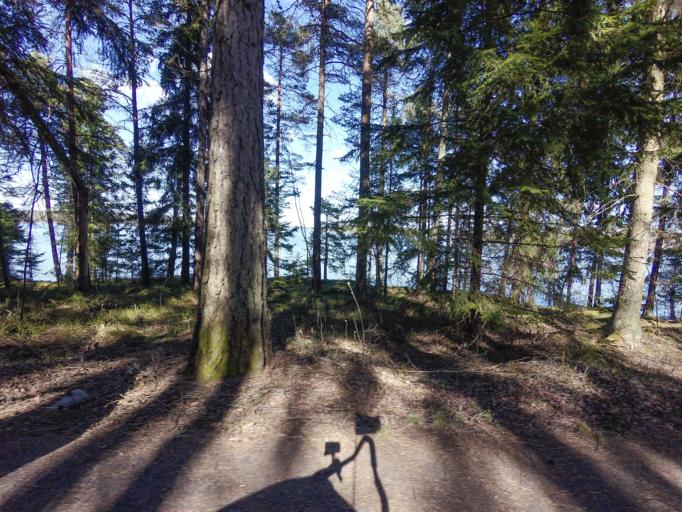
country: FI
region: Uusimaa
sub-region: Helsinki
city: Vantaa
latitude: 60.1713
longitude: 25.0665
